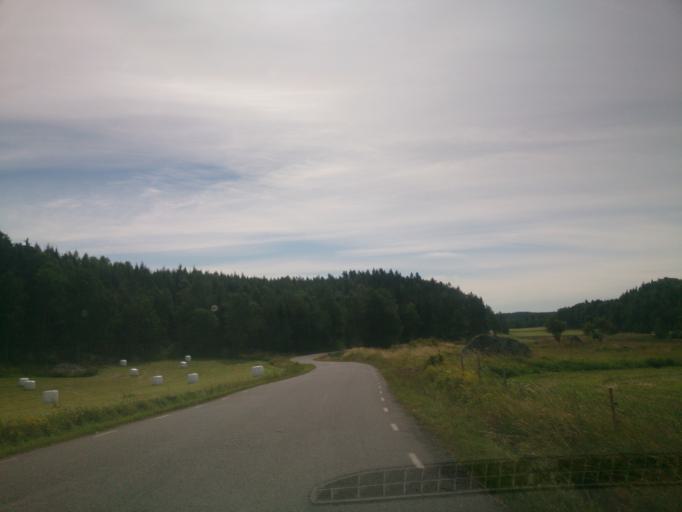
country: SE
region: OEstergoetland
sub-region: Atvidabergs Kommun
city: Atvidaberg
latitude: 58.3225
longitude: 16.0507
